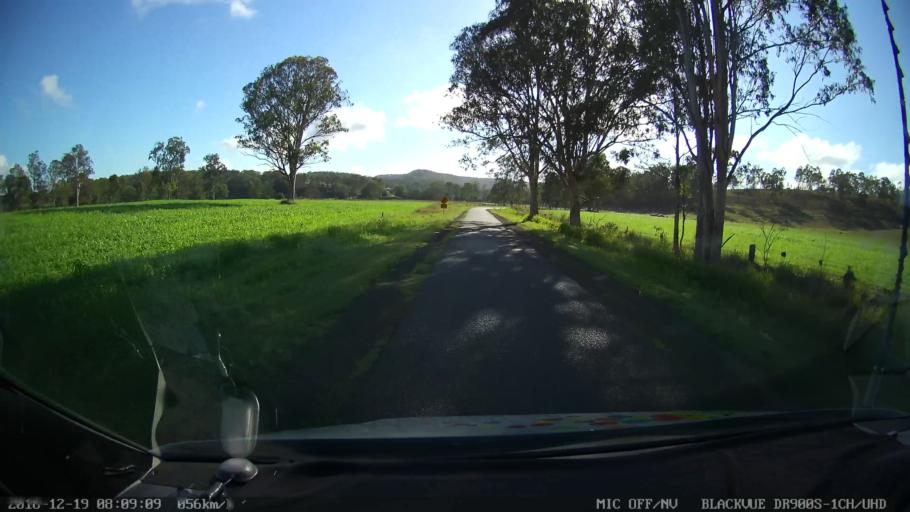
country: AU
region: Queensland
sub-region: Logan
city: Cedar Vale
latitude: -28.2139
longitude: 152.8763
